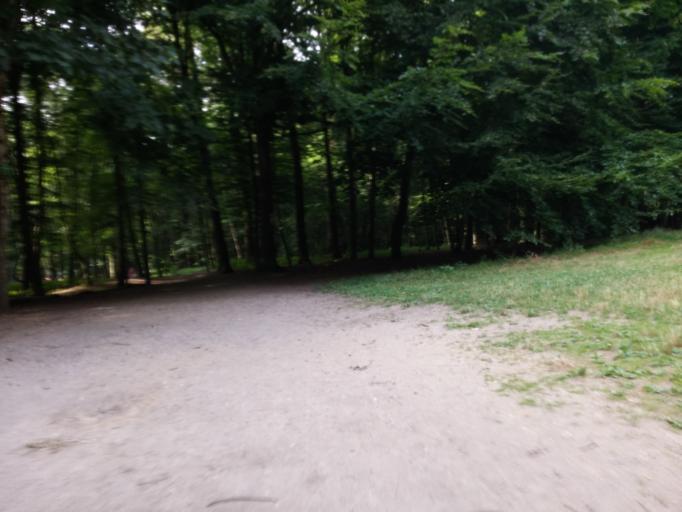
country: DE
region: North Rhine-Westphalia
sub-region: Regierungsbezirk Dusseldorf
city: Krefeld
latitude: 51.3867
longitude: 6.5382
